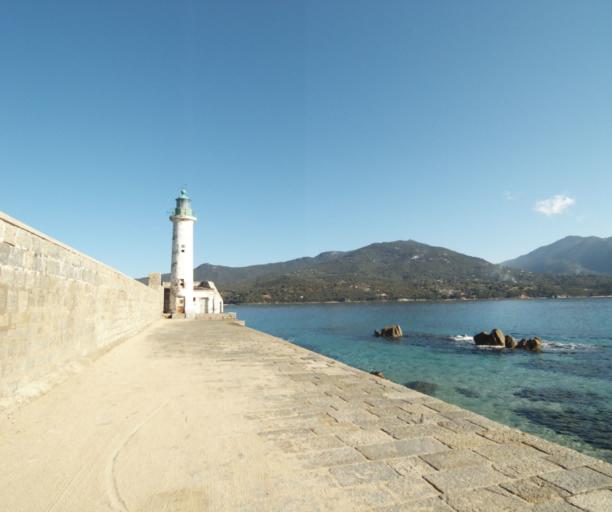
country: FR
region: Corsica
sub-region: Departement de la Corse-du-Sud
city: Propriano
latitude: 41.6781
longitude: 8.8974
